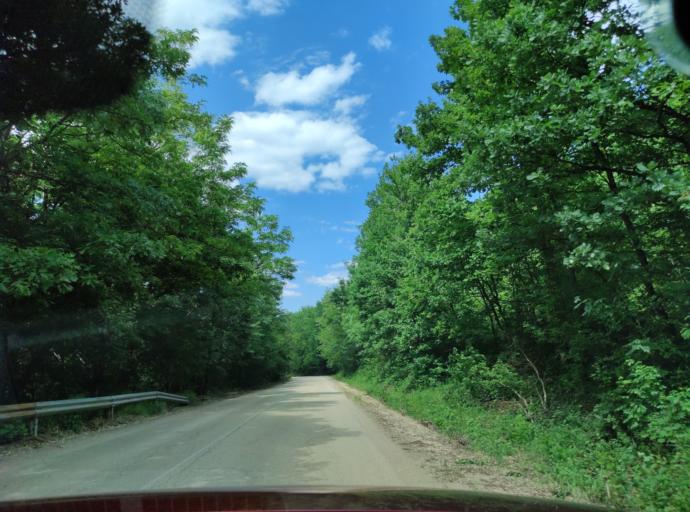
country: BG
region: Montana
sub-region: Obshtina Montana
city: Montana
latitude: 43.3856
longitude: 23.0765
